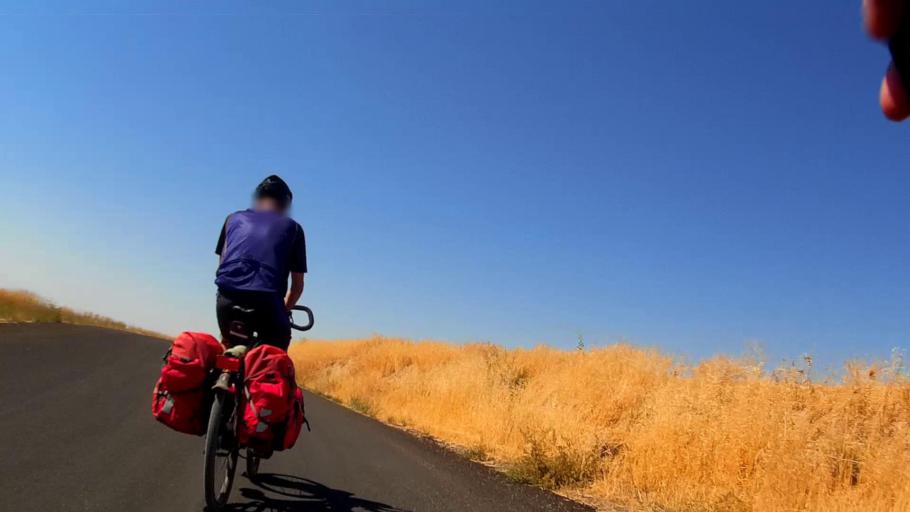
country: US
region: Idaho
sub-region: Madison County
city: Rexburg
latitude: 43.7183
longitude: -111.7441
